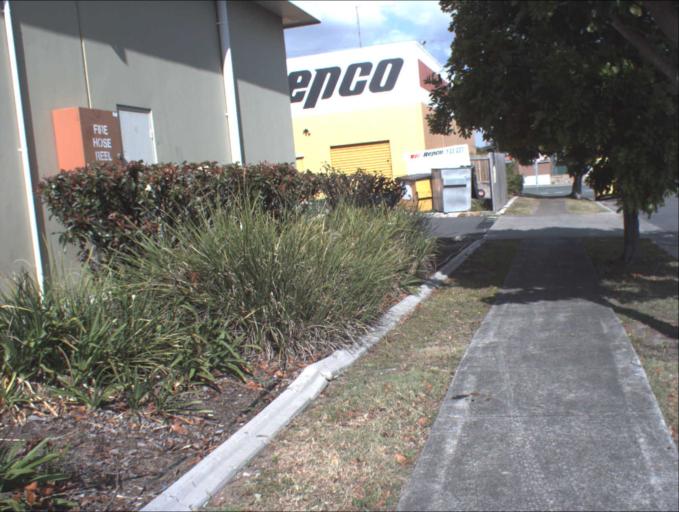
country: AU
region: Queensland
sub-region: Logan
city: Springwood
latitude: -27.6199
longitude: 153.1165
